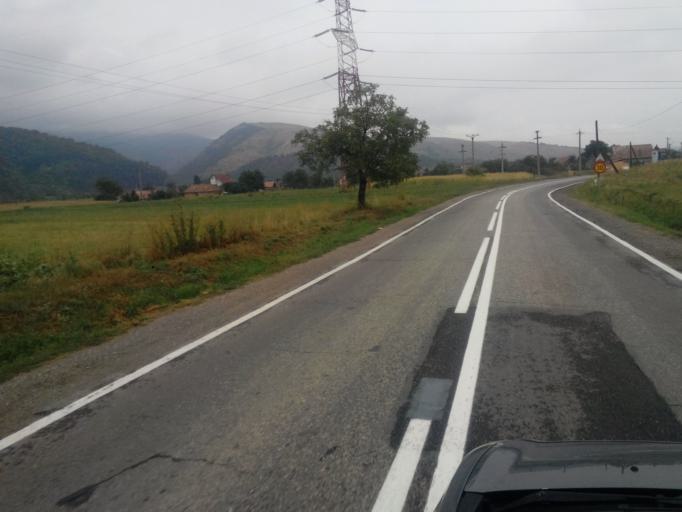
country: RO
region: Cluj
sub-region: Comuna Moldovenesti
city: Moldovenesti
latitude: 46.5171
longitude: 23.6809
